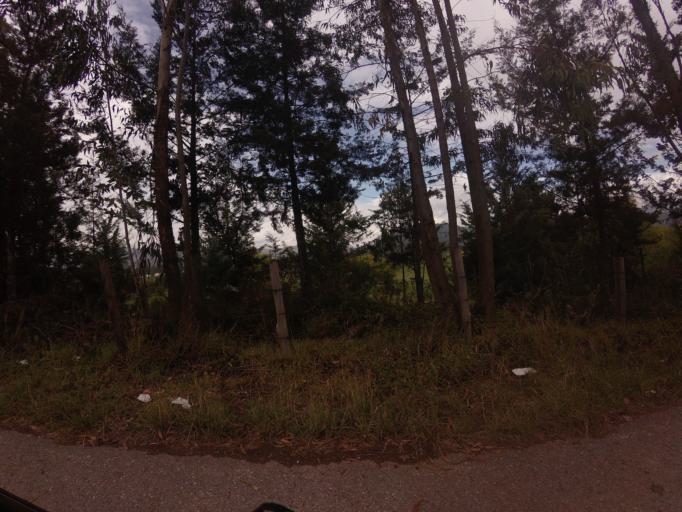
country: CO
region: Boyaca
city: Nobsa
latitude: 5.7893
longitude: -72.9738
